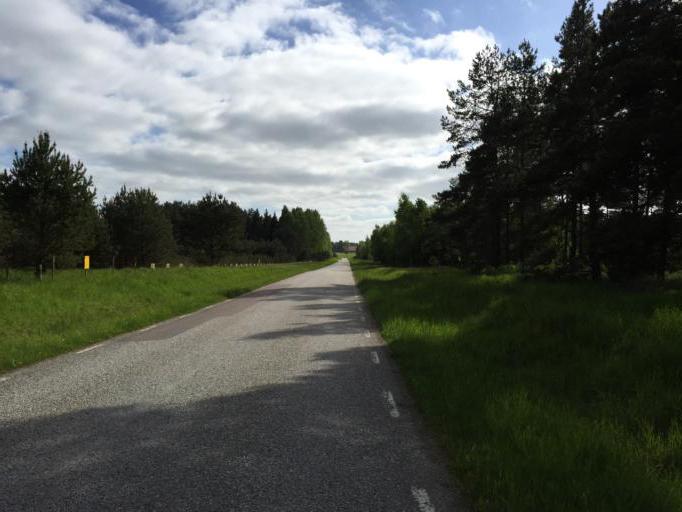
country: SE
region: Skane
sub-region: Sjobo Kommun
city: Blentarp
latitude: 55.6568
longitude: 13.6098
